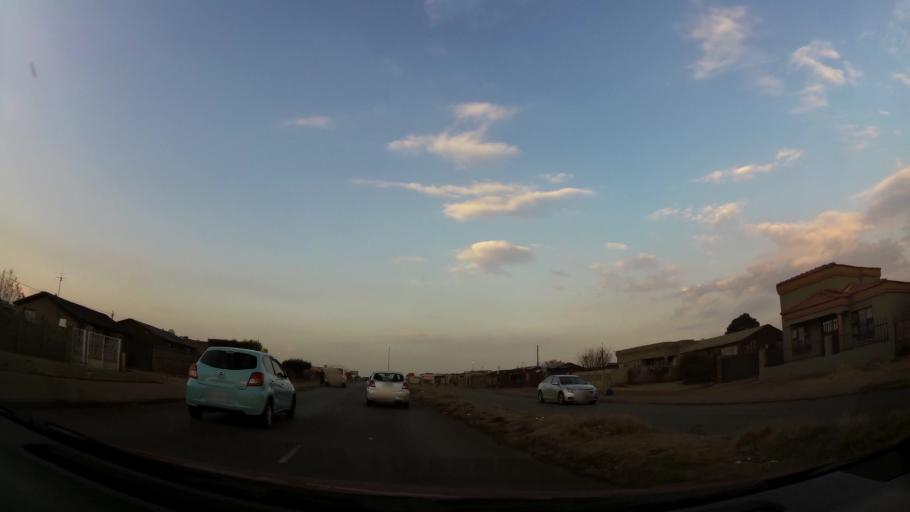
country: ZA
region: Gauteng
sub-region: City of Johannesburg Metropolitan Municipality
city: Orange Farm
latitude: -26.5716
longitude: 27.8407
